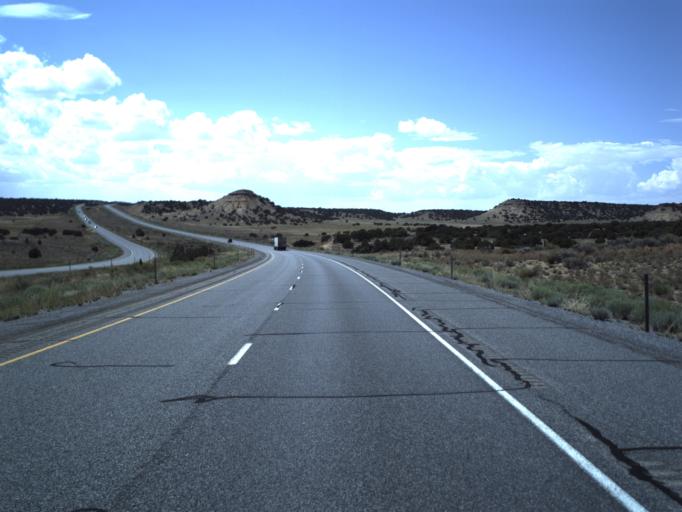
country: US
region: Utah
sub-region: Emery County
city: Castle Dale
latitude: 38.9054
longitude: -110.5522
